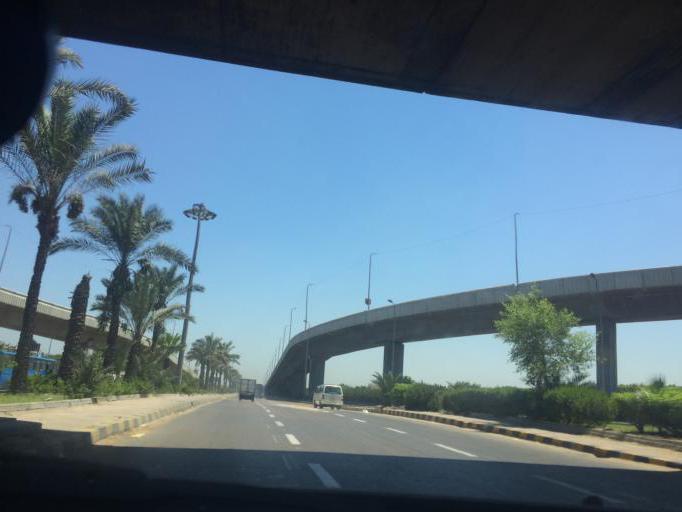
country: EG
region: Alexandria
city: Alexandria
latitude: 31.1807
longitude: 29.9282
